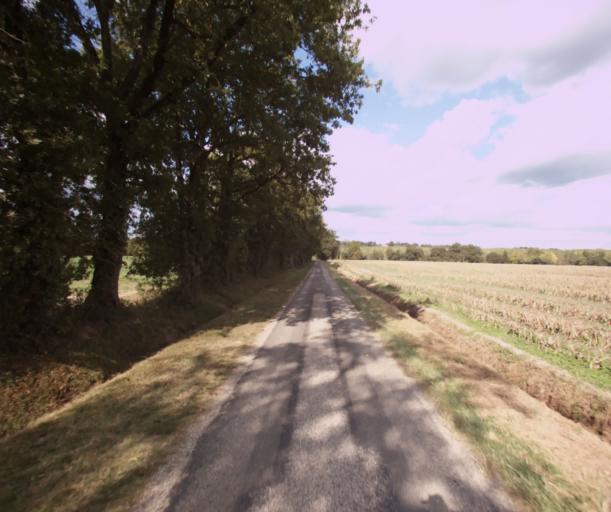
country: FR
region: Midi-Pyrenees
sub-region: Departement du Gers
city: Cazaubon
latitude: 43.9091
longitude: -0.0536
